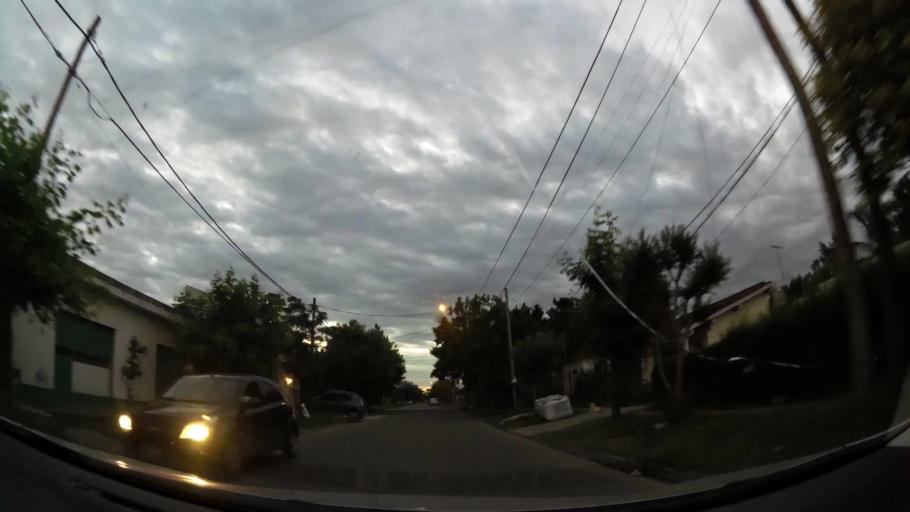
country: AR
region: Buenos Aires
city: Santa Catalina - Dique Lujan
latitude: -34.4141
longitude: -58.6866
